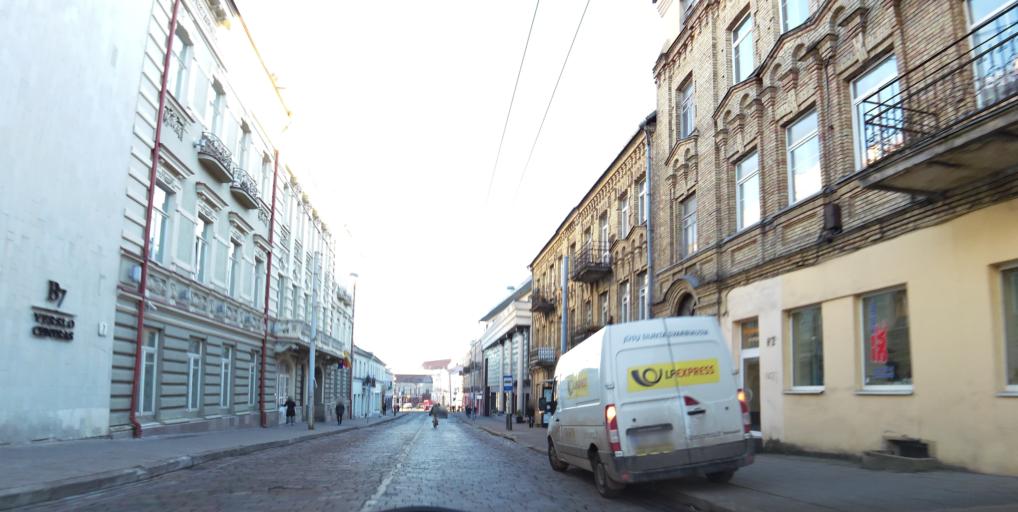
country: LT
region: Vilnius County
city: Naujamiestis
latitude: 54.6801
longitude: 25.2759
